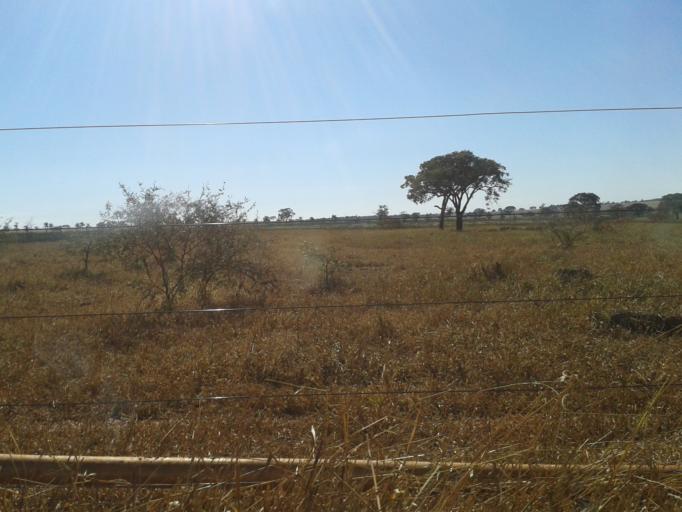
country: BR
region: Minas Gerais
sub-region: Centralina
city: Centralina
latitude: -18.7606
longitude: -49.2027
